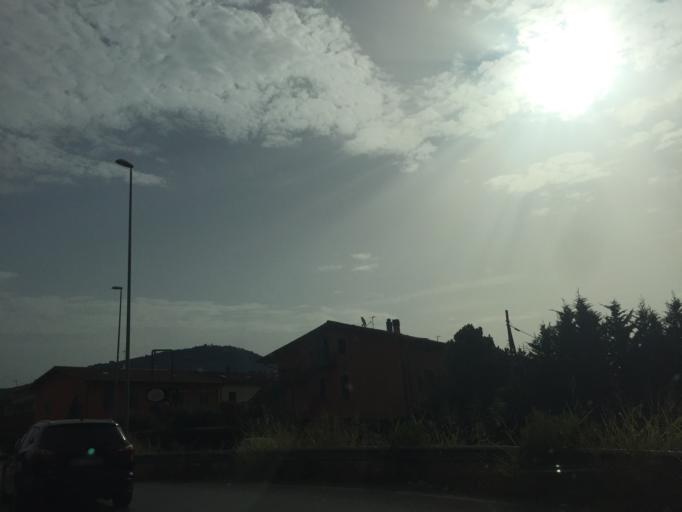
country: IT
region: Tuscany
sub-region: Provincia di Pistoia
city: Monsummano Terme
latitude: 43.8593
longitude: 10.8028
